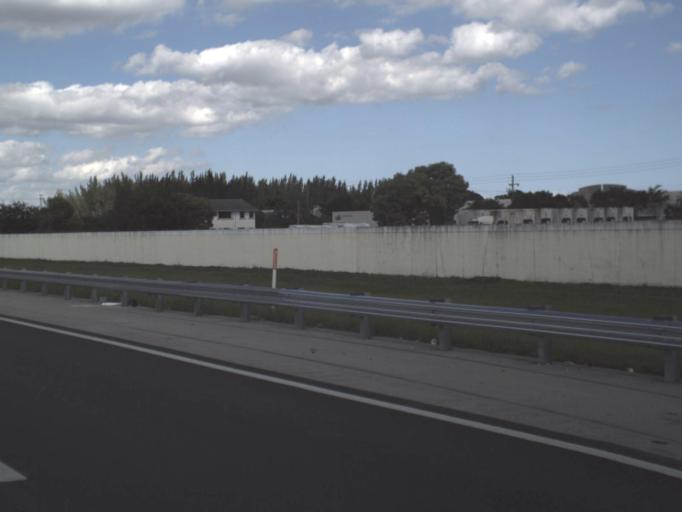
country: US
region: Florida
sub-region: Broward County
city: Davie
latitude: 26.0706
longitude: -80.2154
